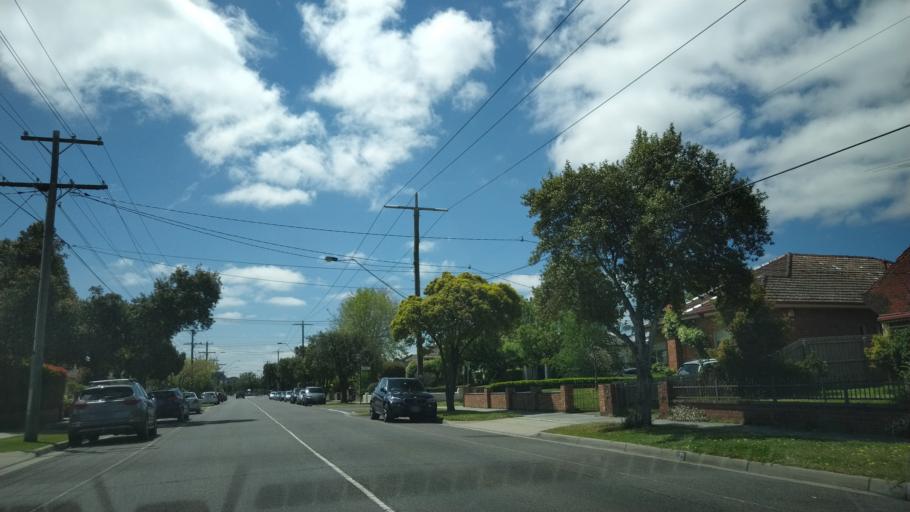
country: AU
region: Victoria
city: Hughesdale
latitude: -37.9004
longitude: 145.0757
